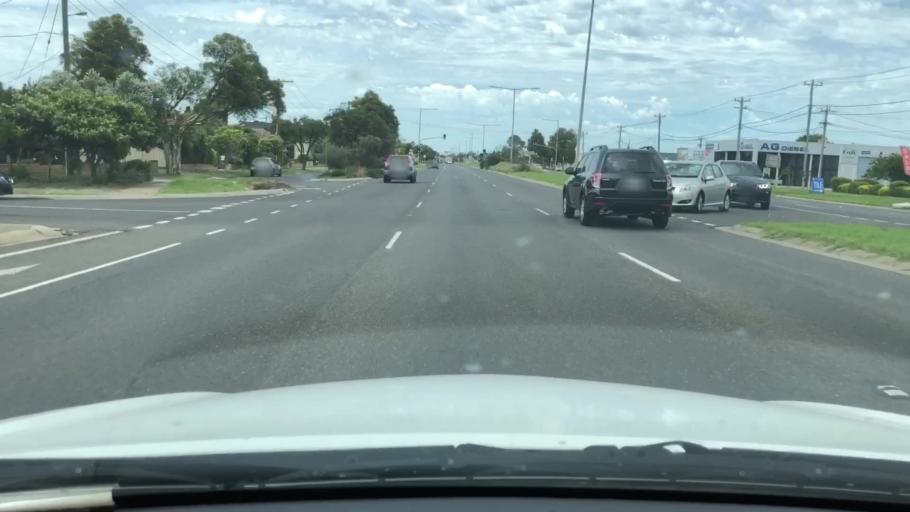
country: AU
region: Victoria
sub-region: Greater Dandenong
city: Springvale
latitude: -37.9503
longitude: 145.1386
